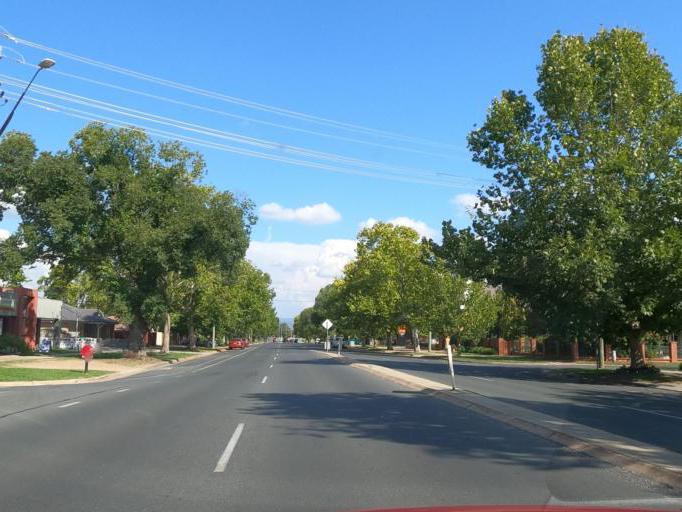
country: AU
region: New South Wales
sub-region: Albury Municipality
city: North Albury
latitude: -36.0643
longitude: 146.9246
